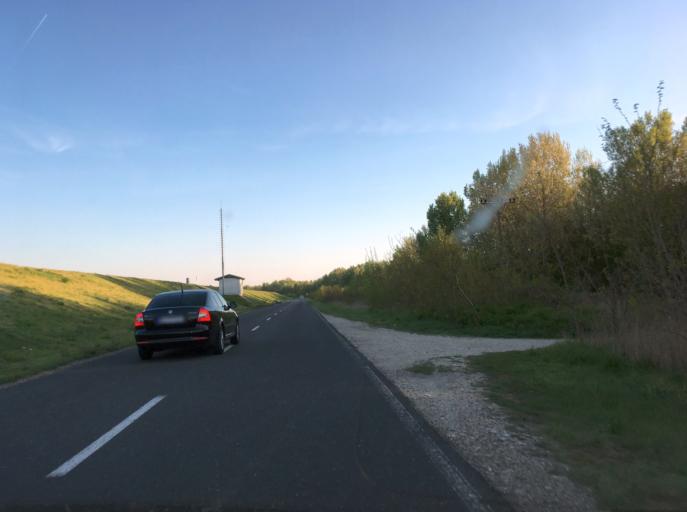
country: HU
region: Gyor-Moson-Sopron
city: Rajka
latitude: 48.0129
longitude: 17.2519
